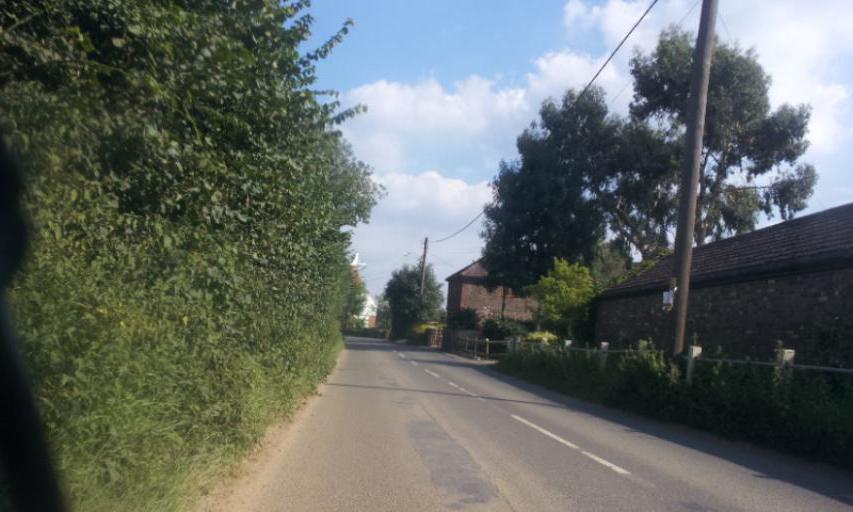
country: GB
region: England
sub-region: Kent
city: Yalding
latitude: 51.2172
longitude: 0.4498
